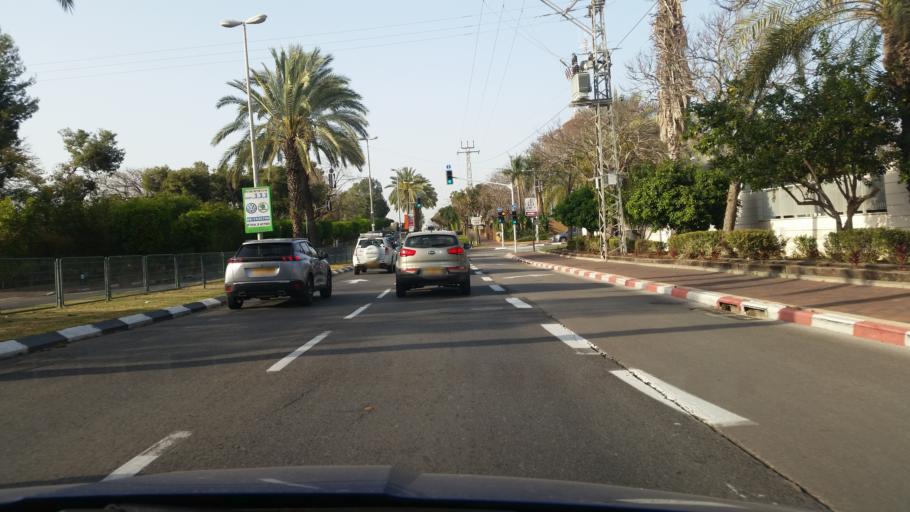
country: IL
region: Central District
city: Ra'anana
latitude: 32.1867
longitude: 34.8545
